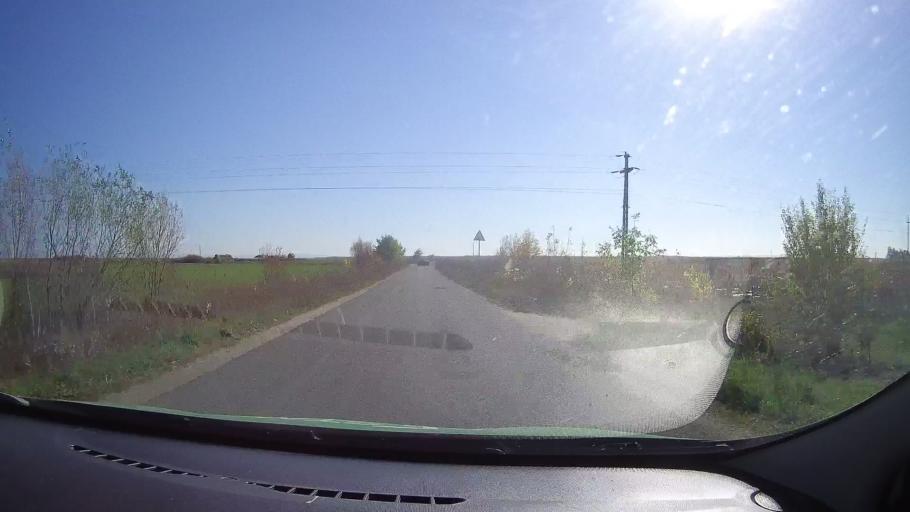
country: RO
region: Satu Mare
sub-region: Comuna Doba
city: Doba
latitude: 47.7397
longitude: 22.7175
